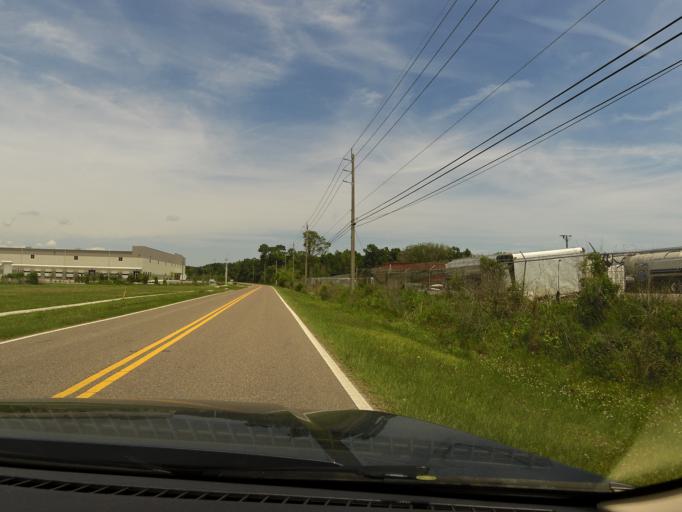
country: US
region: Florida
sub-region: Duval County
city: Jacksonville
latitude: 30.4534
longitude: -81.5581
